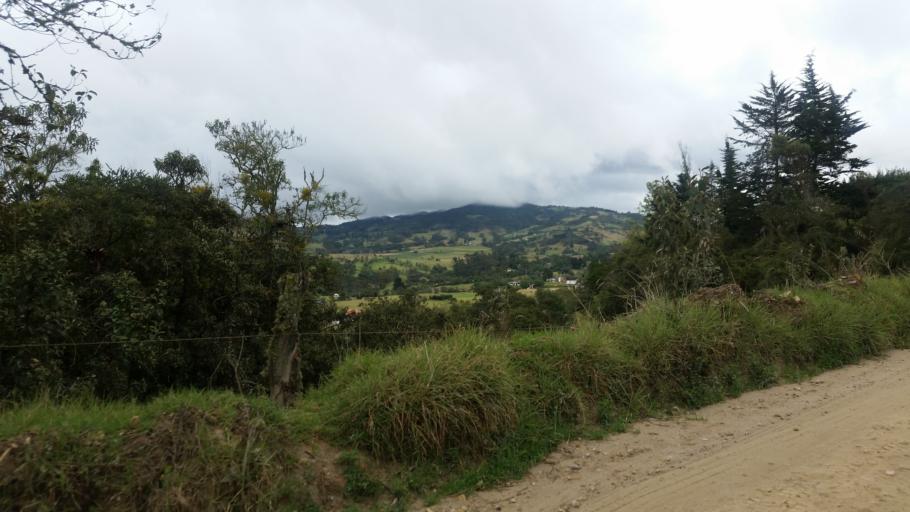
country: CO
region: Cundinamarca
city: La Calera
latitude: 4.7143
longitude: -73.9365
